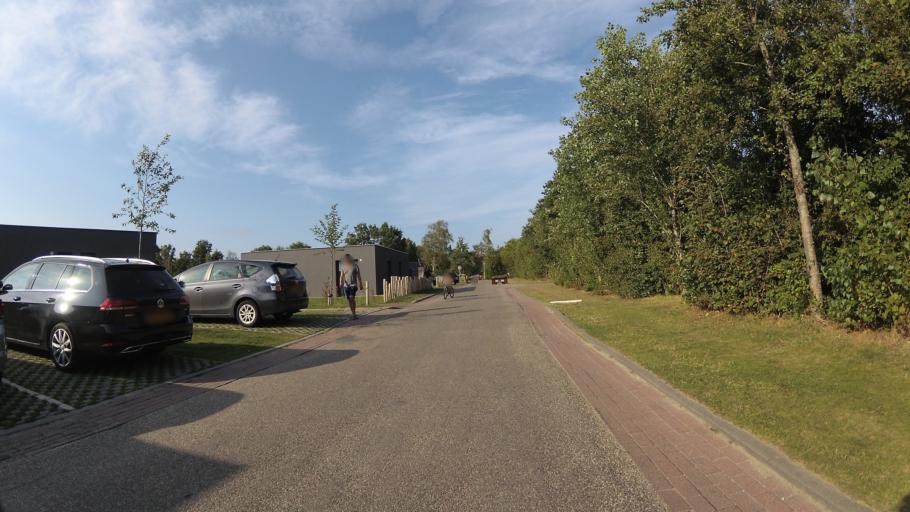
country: NL
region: Zeeland
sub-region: Gemeente Veere
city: Veere
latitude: 51.5696
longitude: 3.6633
